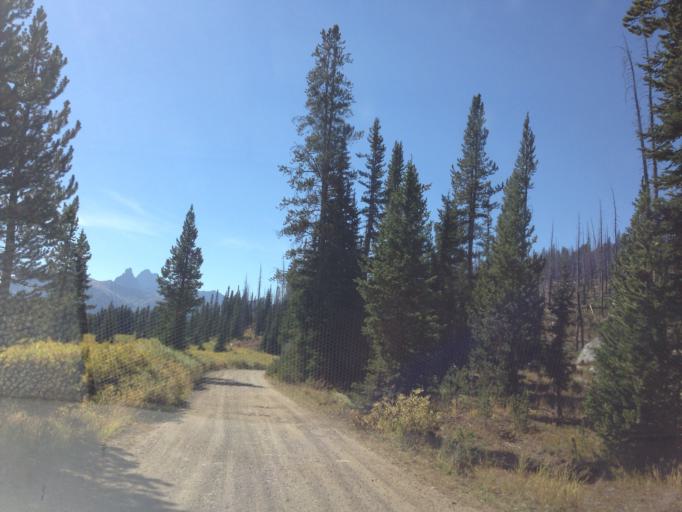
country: US
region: Montana
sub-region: Stillwater County
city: Absarokee
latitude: 45.0496
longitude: -109.9141
